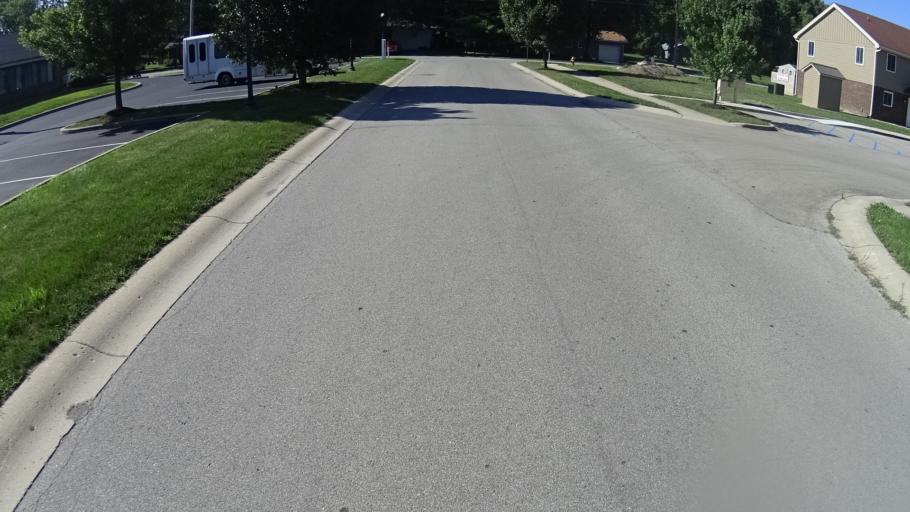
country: US
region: Indiana
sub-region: Madison County
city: Pendleton
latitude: 40.0042
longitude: -85.7337
